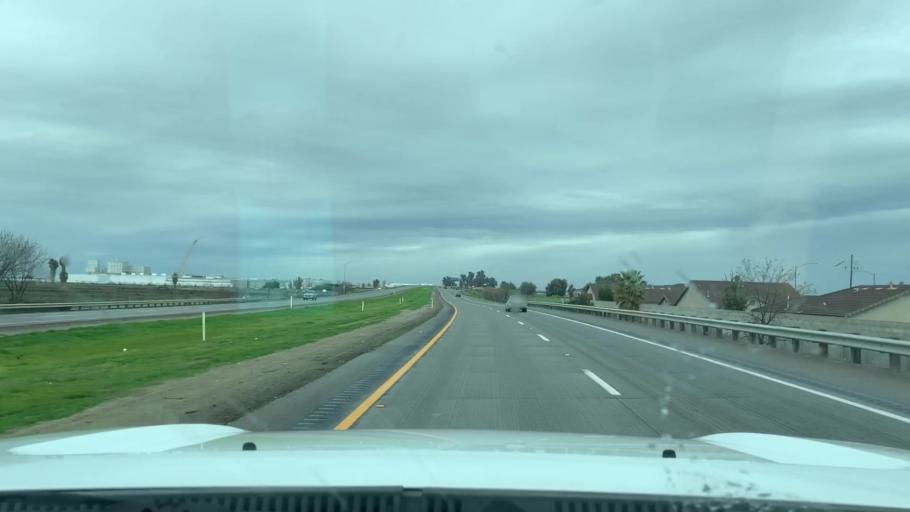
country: US
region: California
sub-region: Kings County
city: Lemoore
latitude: 36.2897
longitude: -119.8082
